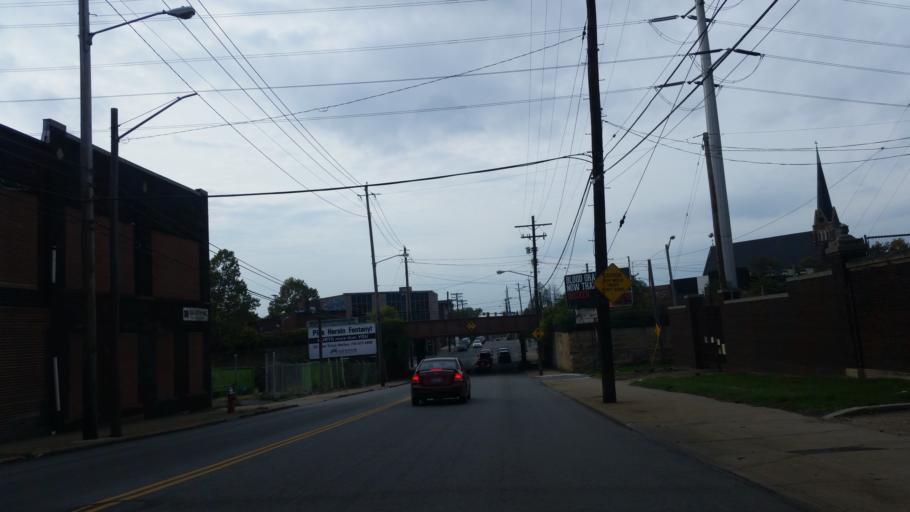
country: US
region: Ohio
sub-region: Cuyahoga County
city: Newburgh Heights
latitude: 41.4489
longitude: -81.6261
